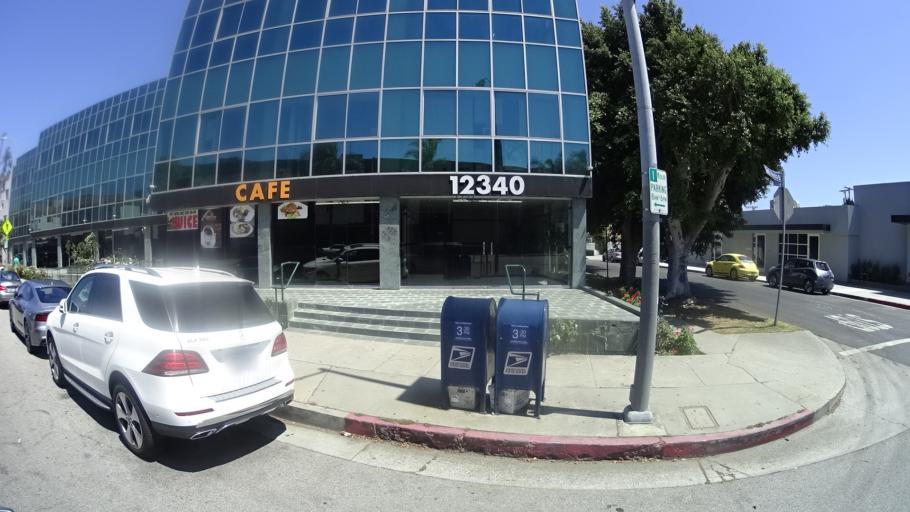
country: US
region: California
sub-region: Los Angeles County
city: Santa Monica
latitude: 34.0390
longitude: -118.4664
